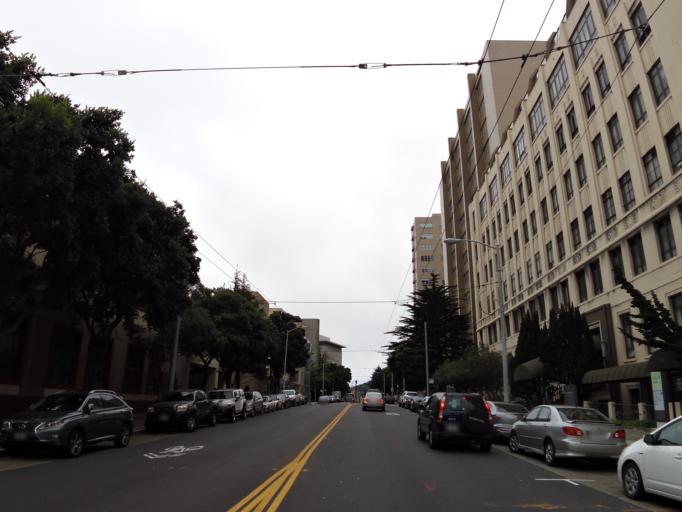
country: US
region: California
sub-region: San Francisco County
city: San Francisco
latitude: 37.7631
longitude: -122.4594
